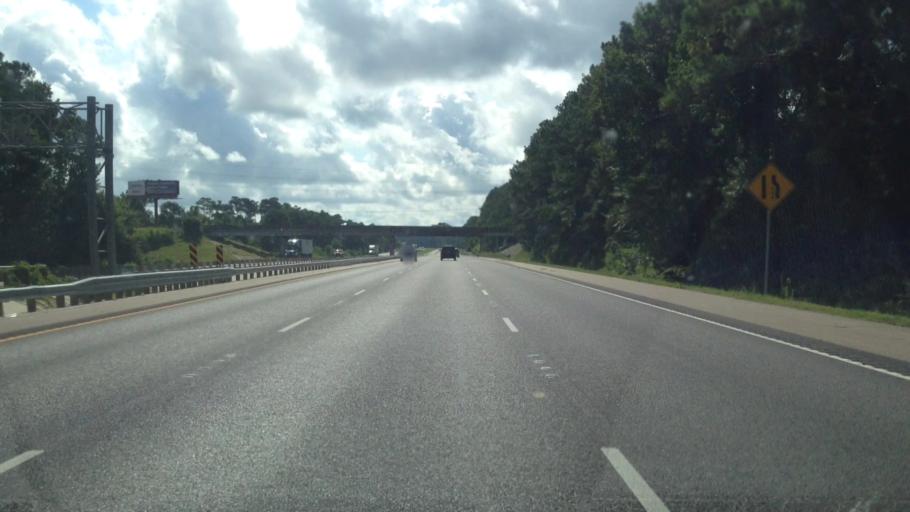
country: US
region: Louisiana
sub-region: Saint Tammany Parish
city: Slidell
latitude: 30.3020
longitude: -89.7267
